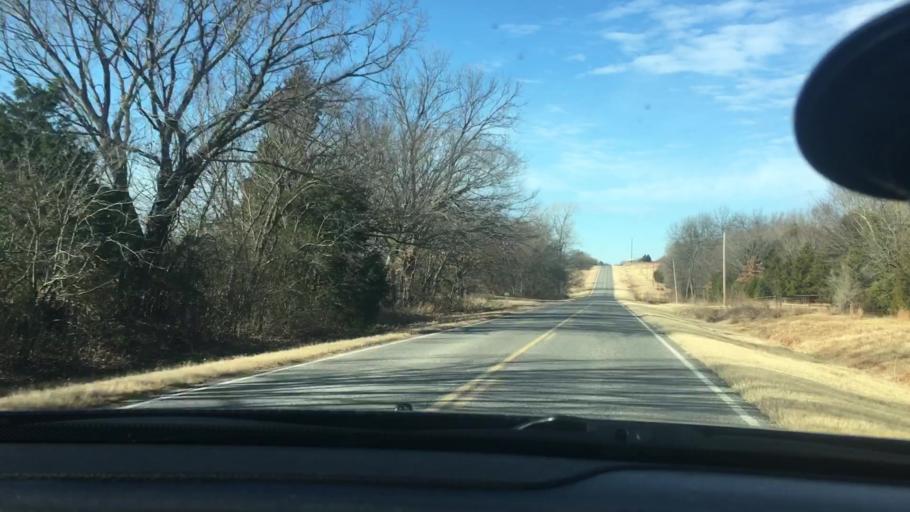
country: US
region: Oklahoma
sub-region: Seminole County
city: Konawa
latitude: 34.9856
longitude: -96.8021
